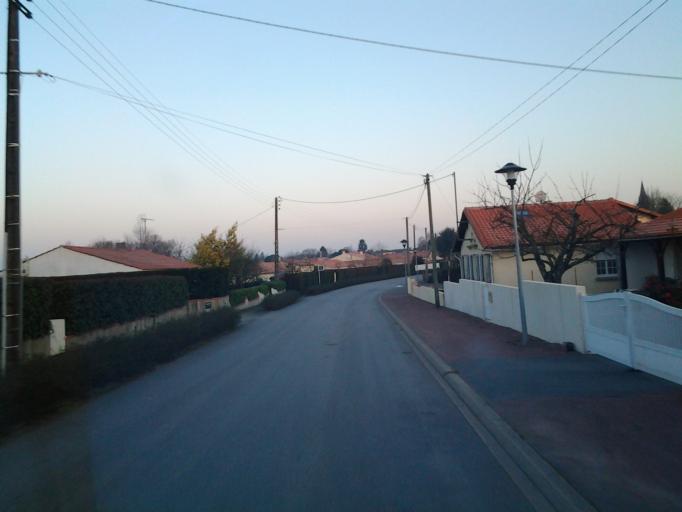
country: FR
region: Pays de la Loire
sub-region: Departement de la Vendee
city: La Chaize-le-Vicomte
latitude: 46.6556
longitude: -1.2307
